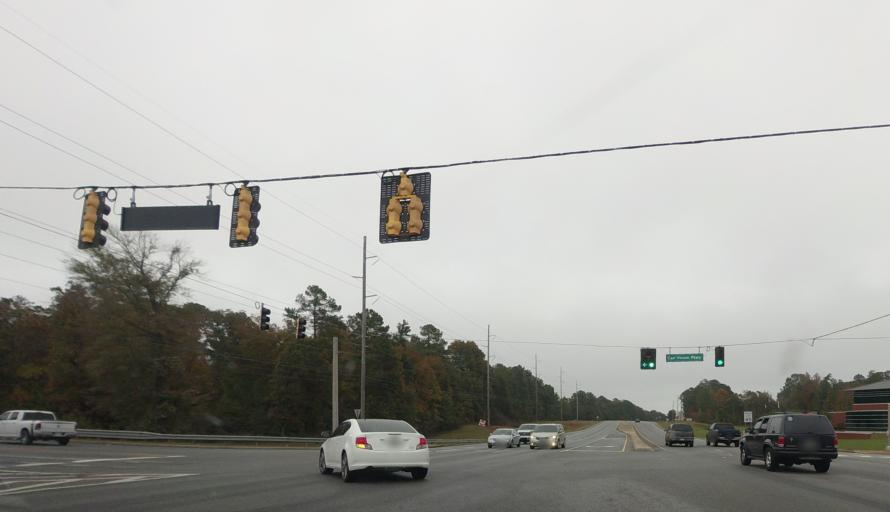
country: US
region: Georgia
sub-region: Houston County
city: Centerville
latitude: 32.5931
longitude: -83.6653
